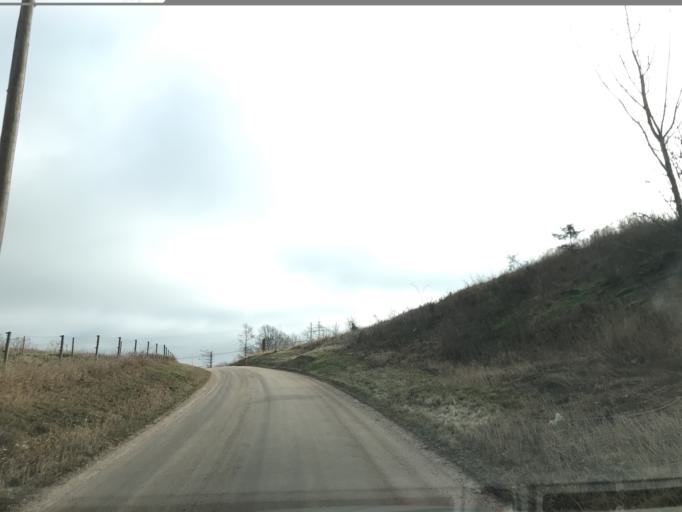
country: SE
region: Skane
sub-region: Svalovs Kommun
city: Teckomatorp
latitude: 55.8341
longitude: 13.0673
